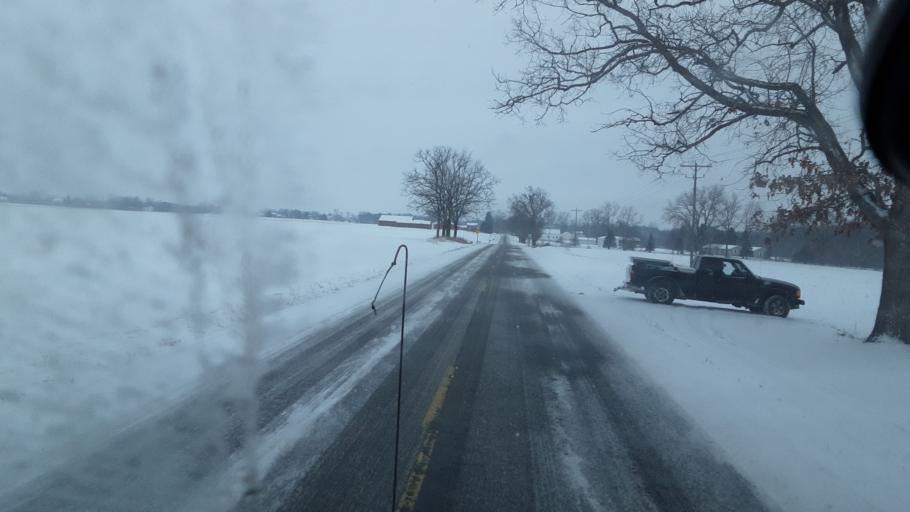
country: US
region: Michigan
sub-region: Ingham County
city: Leslie
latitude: 42.4343
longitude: -84.3168
